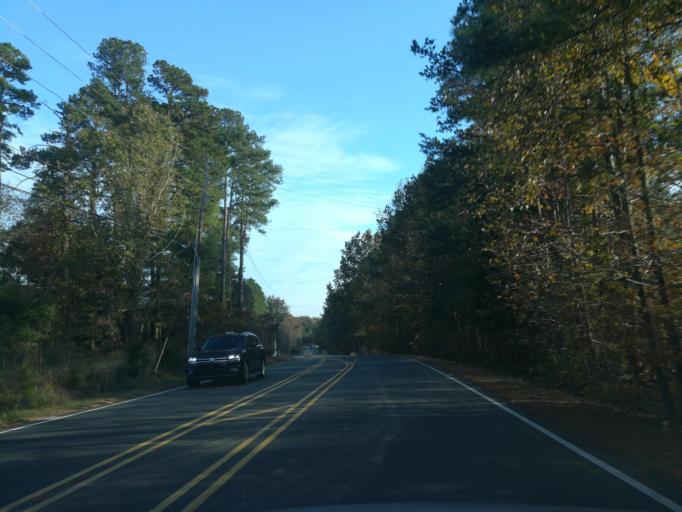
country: US
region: North Carolina
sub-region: Orange County
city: Chapel Hill
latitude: 35.9612
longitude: -78.9993
